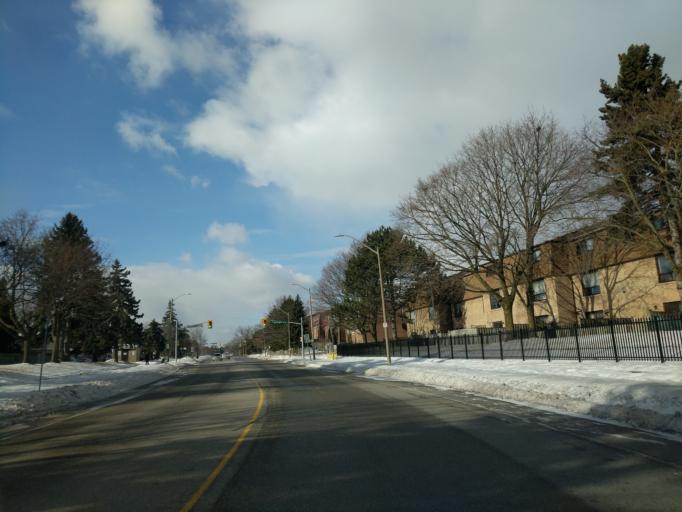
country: CA
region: Ontario
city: Ajax
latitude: 43.8394
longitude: -79.0891
